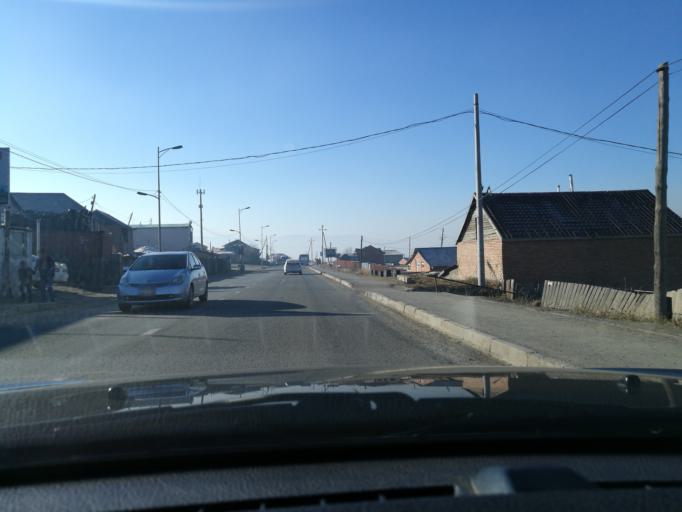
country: MN
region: Ulaanbaatar
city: Ulaanbaatar
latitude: 47.9726
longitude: 106.9310
